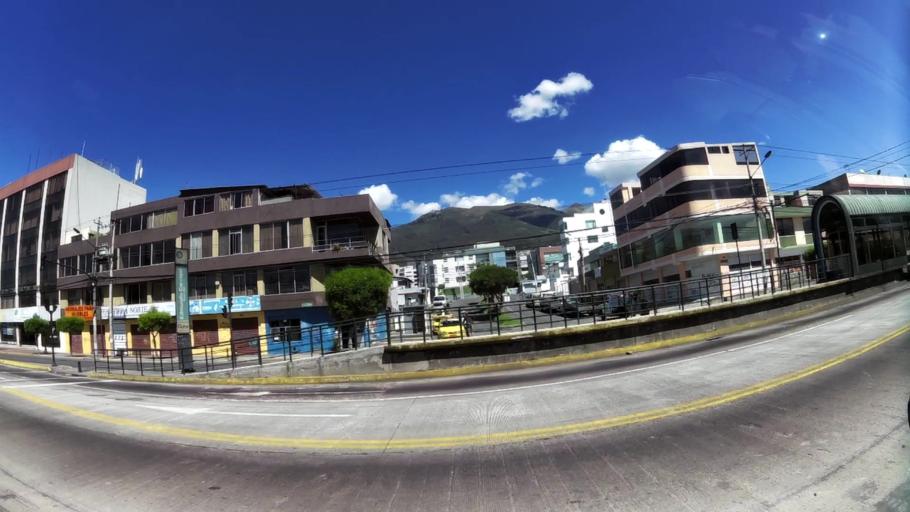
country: EC
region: Pichincha
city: Quito
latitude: -0.1586
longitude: -78.4879
